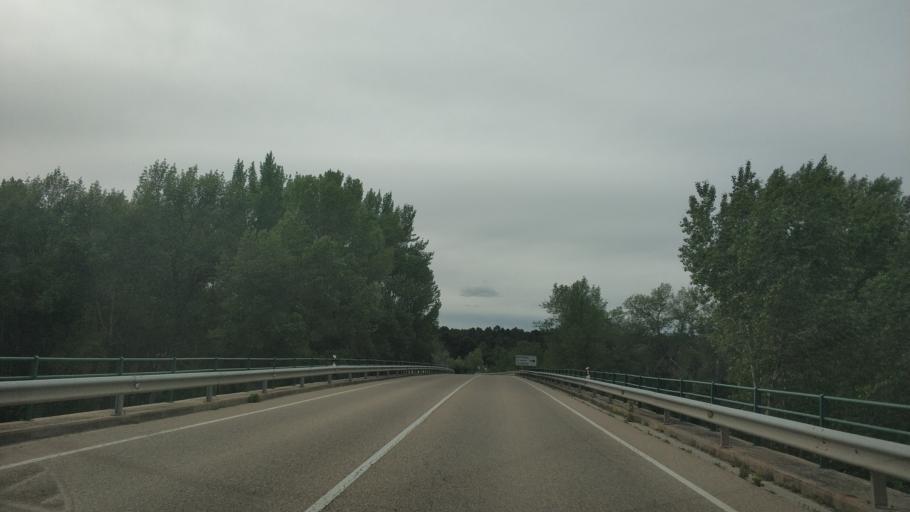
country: ES
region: Castille and Leon
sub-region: Provincia de Soria
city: Bayubas de Abajo
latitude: 41.5022
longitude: -2.8878
